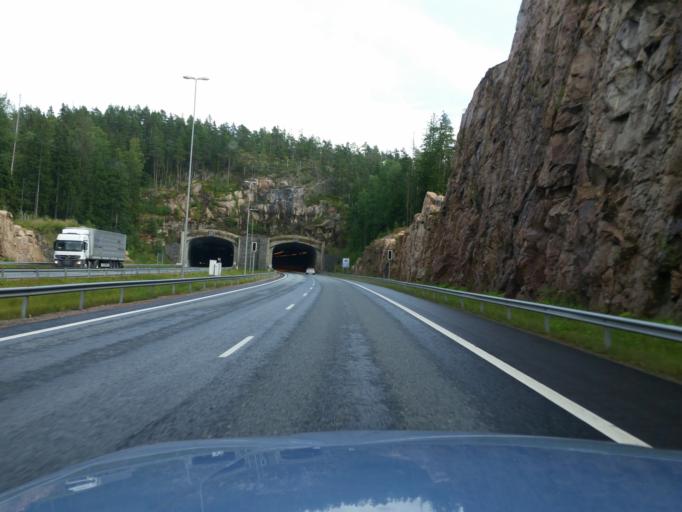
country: FI
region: Uusimaa
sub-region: Helsinki
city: Saukkola
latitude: 60.3270
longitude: 23.9398
